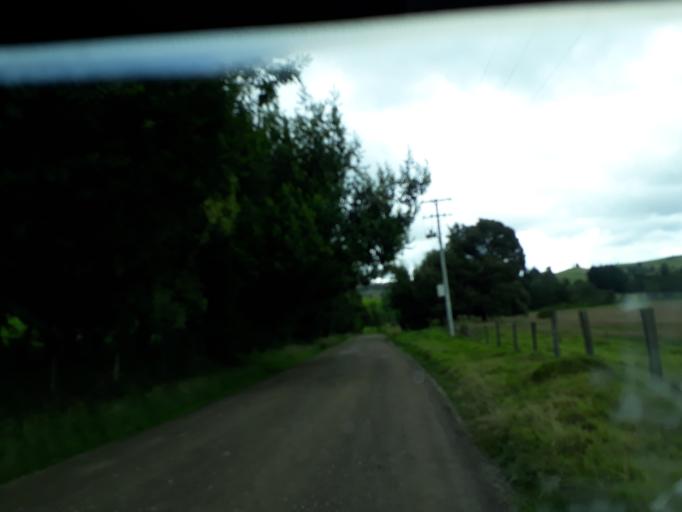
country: CO
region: Cundinamarca
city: La Mesa
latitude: 5.2007
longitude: -73.9243
